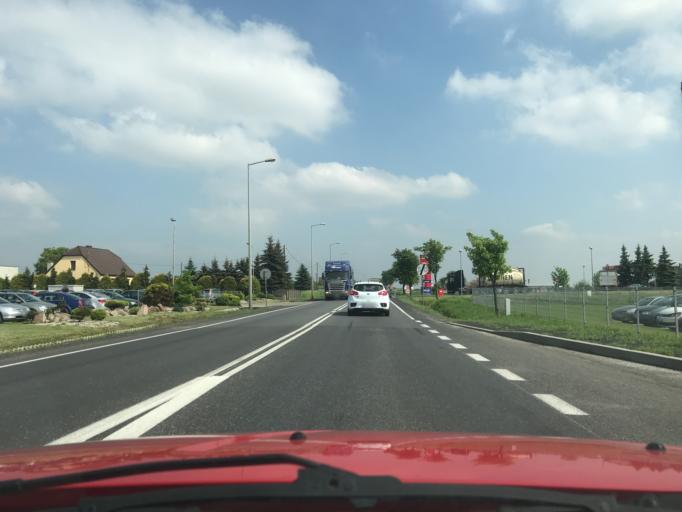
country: PL
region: Greater Poland Voivodeship
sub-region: Powiat pleszewski
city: Czermin
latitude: 51.9051
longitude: 17.7383
